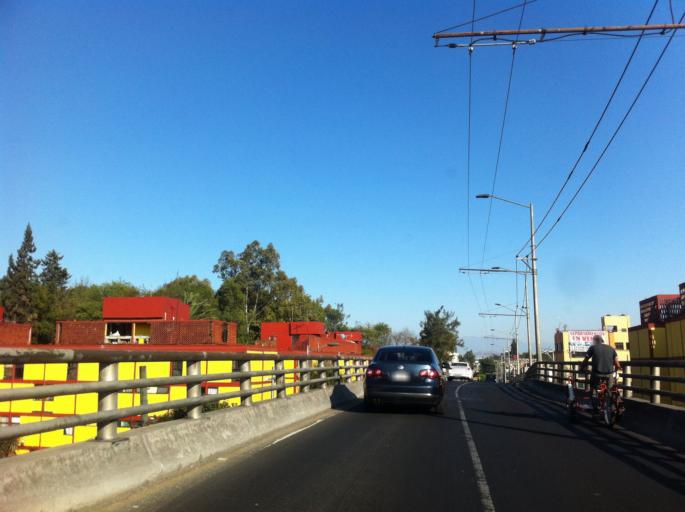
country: MX
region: Mexico City
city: Mexico City
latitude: 19.4138
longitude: -99.1140
